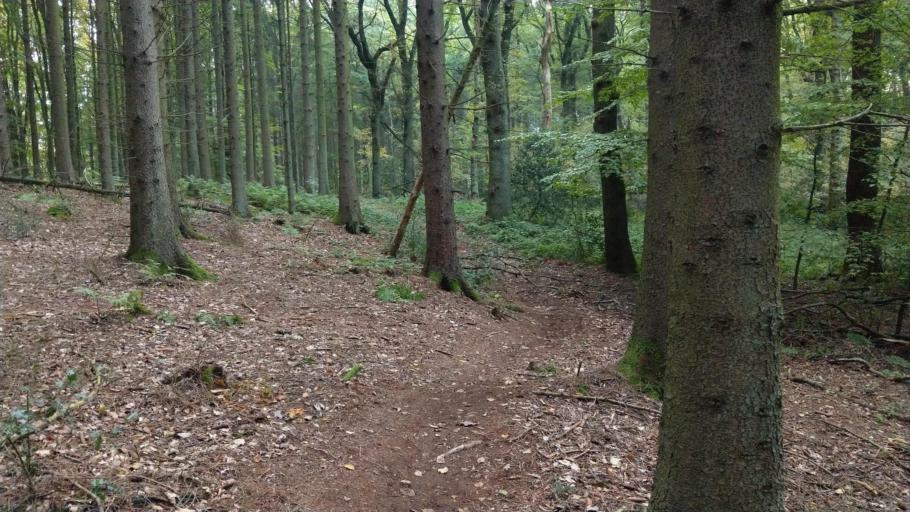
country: NL
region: Limburg
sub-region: Gemeente Vaals
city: Vaals
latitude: 50.7550
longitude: 6.0430
